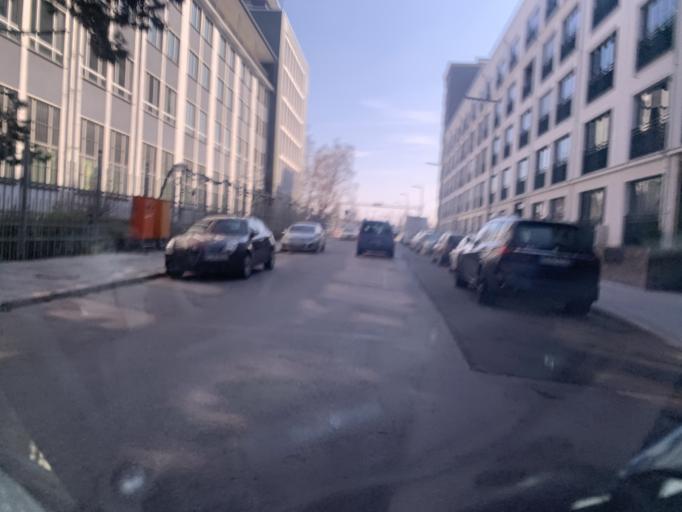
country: DE
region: Bavaria
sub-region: Upper Bavaria
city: Bogenhausen
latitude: 48.1390
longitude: 11.6200
